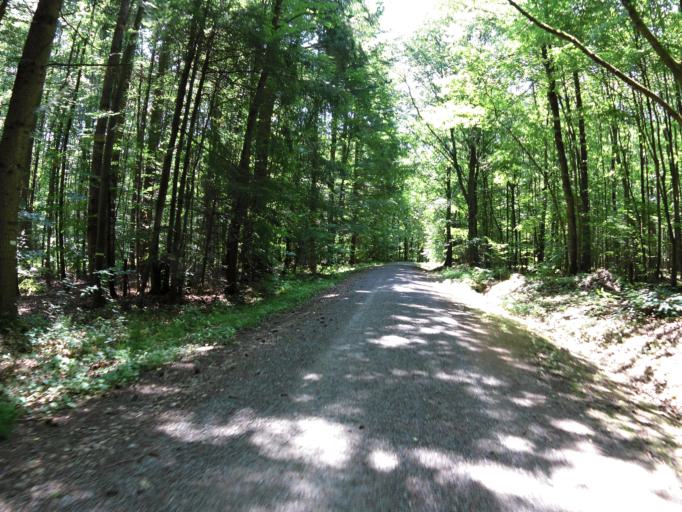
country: DE
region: Bavaria
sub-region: Regierungsbezirk Unterfranken
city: Kleinrinderfeld
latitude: 49.7188
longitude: 9.8557
